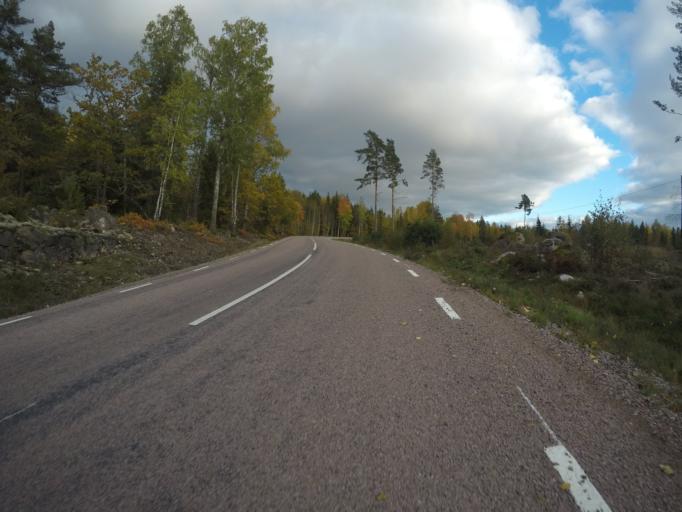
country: SE
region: Vaestmanland
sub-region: Arboga Kommun
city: Tyringe
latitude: 59.3099
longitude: 15.9905
